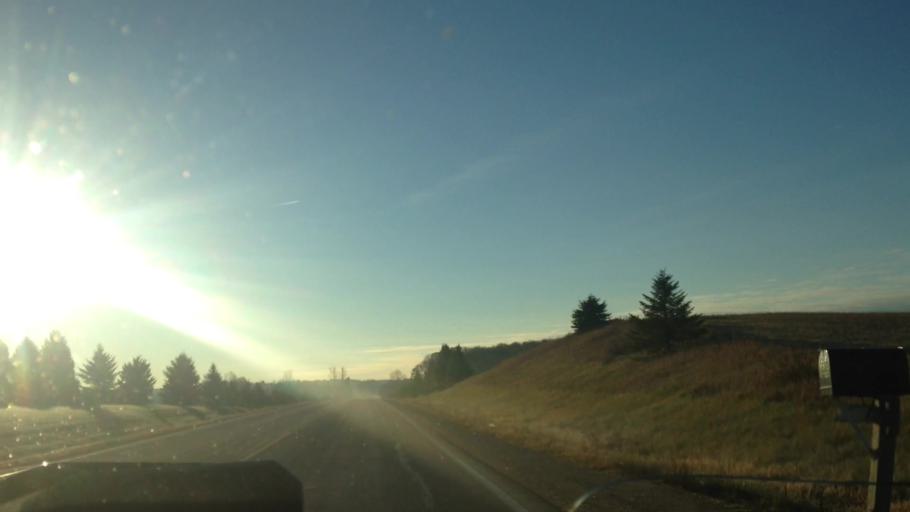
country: US
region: Wisconsin
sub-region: Dodge County
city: Mayville
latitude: 43.4859
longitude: -88.5131
